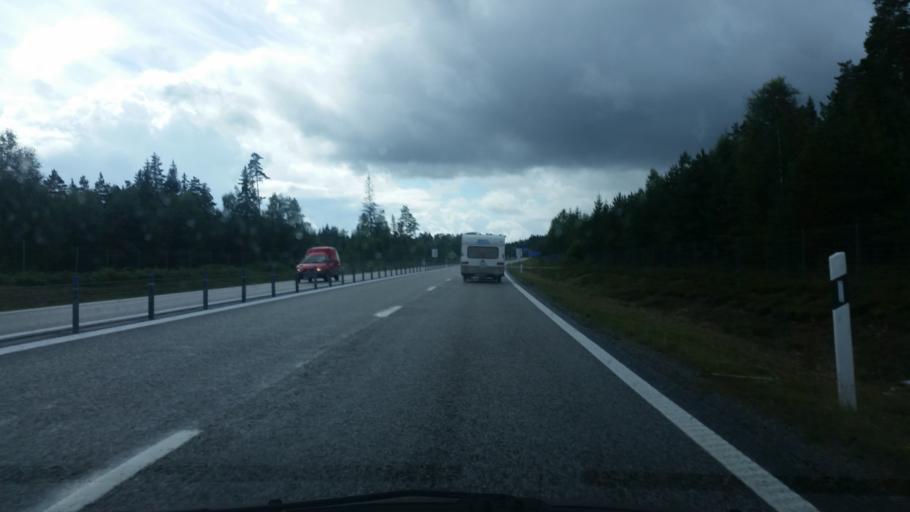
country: SE
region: Joenkoeping
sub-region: Gislaveds Kommun
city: Gislaved
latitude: 57.3471
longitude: 13.5552
